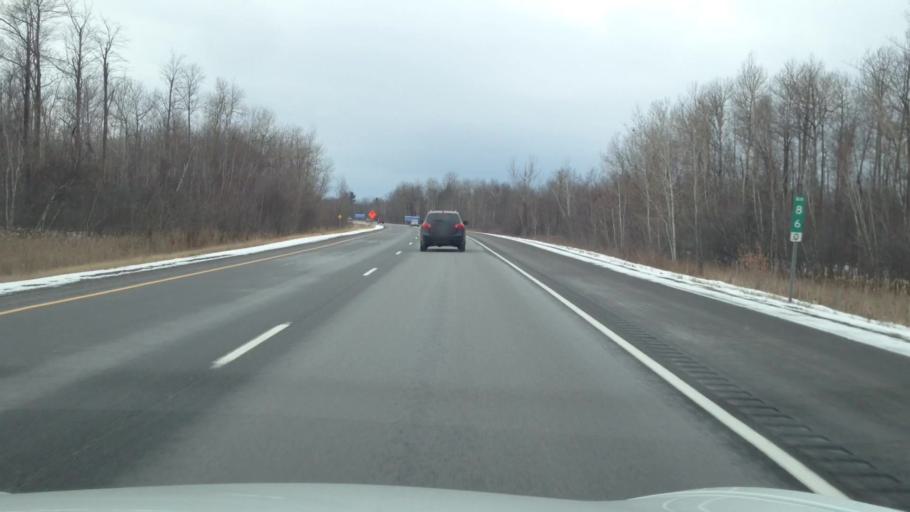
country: CA
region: Ontario
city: Bourget
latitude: 45.3349
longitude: -75.3170
